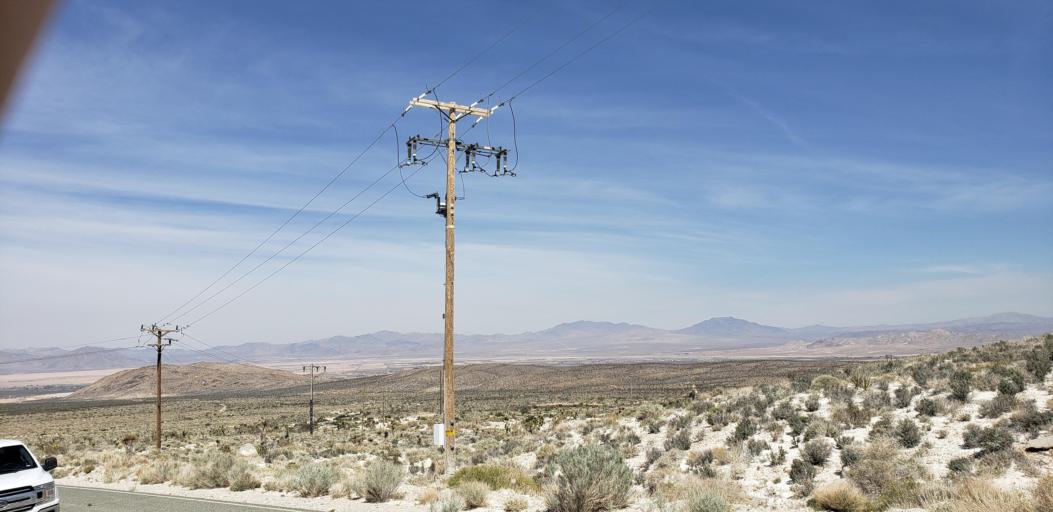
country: US
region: California
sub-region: San Bernardino County
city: Lucerne Valley
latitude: 34.3694
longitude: -116.9071
